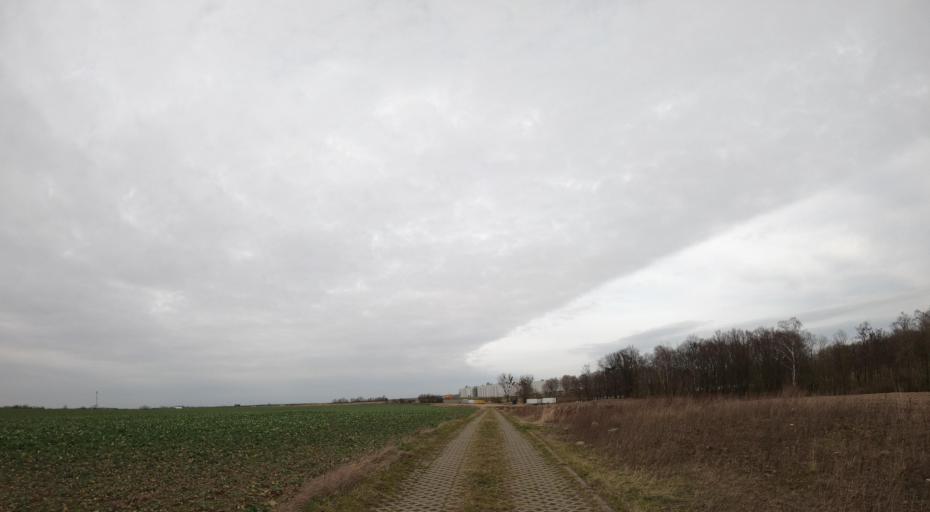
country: PL
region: West Pomeranian Voivodeship
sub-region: Powiat pyrzycki
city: Bielice
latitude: 53.2552
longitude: 14.6391
